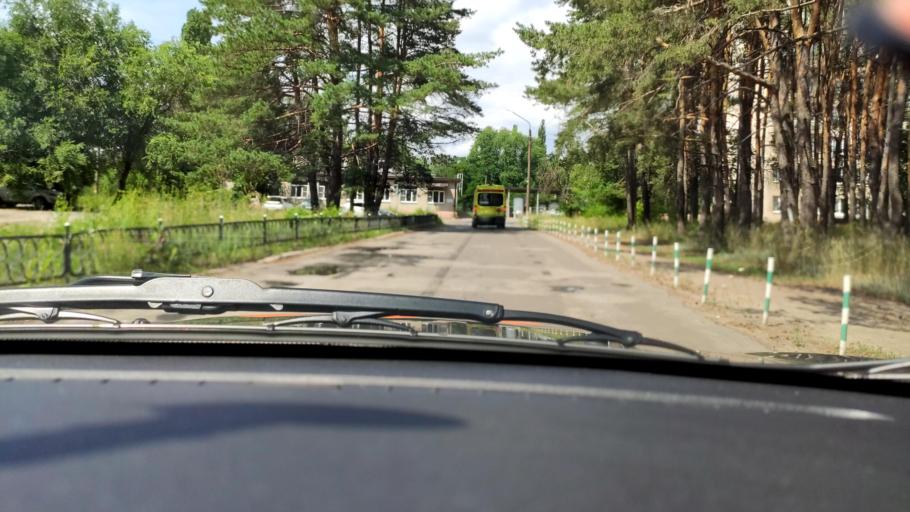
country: RU
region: Voronezj
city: Podgornoye
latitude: 51.7434
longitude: 39.1778
